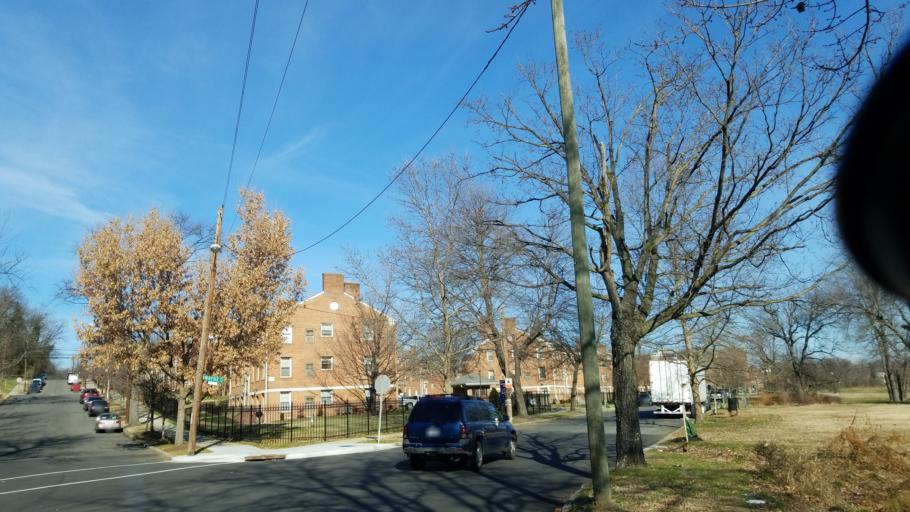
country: US
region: Maryland
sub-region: Prince George's County
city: Glassmanor
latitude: 38.8339
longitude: -77.0028
